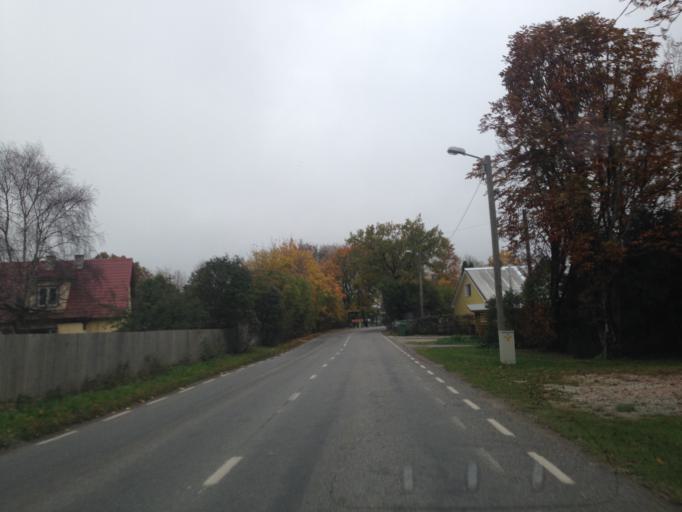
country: EE
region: Harju
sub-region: Saue linn
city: Saue
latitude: 59.3257
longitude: 24.5475
